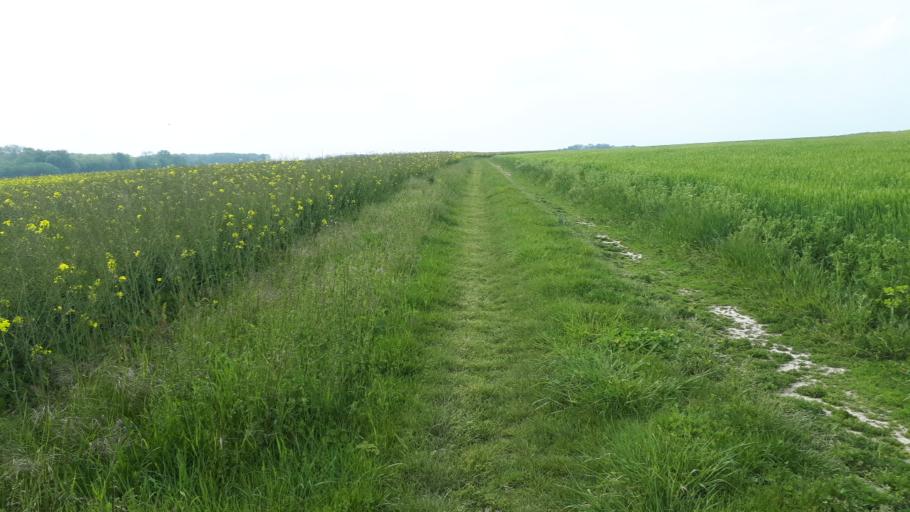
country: FR
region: Centre
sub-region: Departement du Loir-et-Cher
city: Lunay
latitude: 47.8258
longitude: 0.9318
